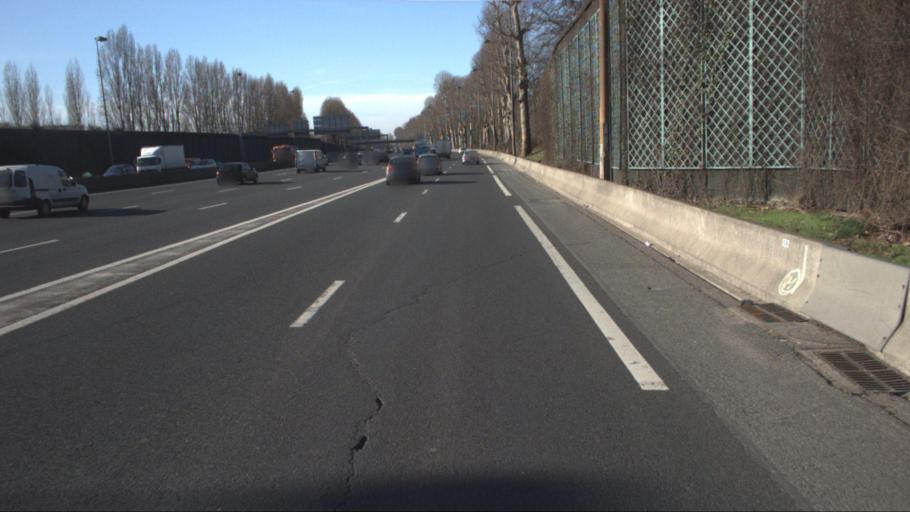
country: FR
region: Ile-de-France
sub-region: Departement du Val-de-Marne
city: Maisons-Alfort
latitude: 48.8176
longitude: 2.4409
